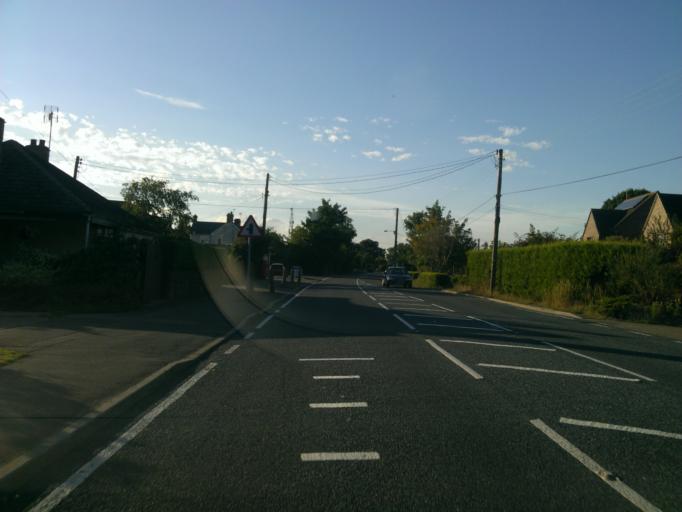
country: GB
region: England
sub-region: Essex
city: Alresford
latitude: 51.8571
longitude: 1.0000
